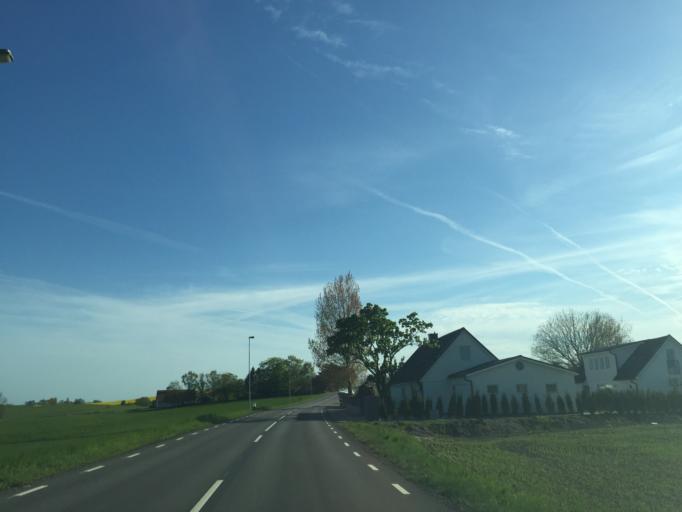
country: SE
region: Skane
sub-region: Malmo
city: Oxie
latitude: 55.5680
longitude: 13.1158
